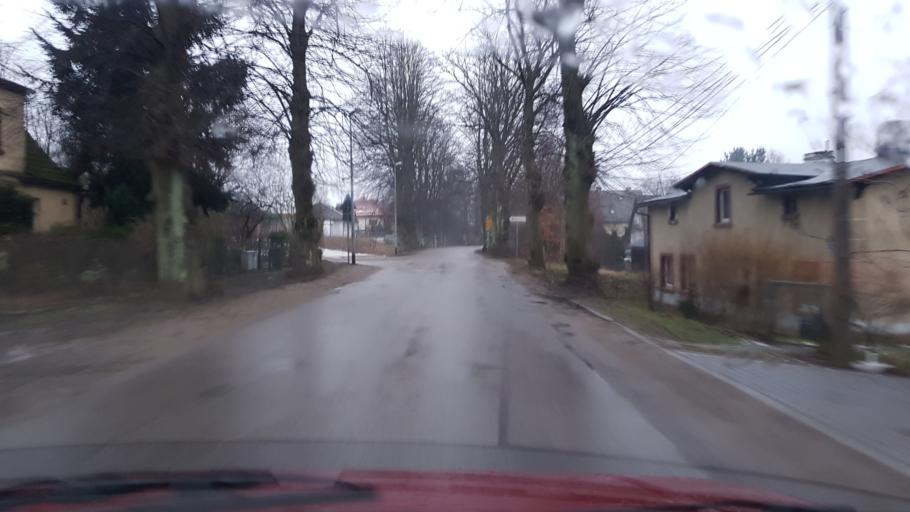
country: PL
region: West Pomeranian Voivodeship
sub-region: Powiat koszalinski
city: Sianow
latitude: 54.1846
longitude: 16.2442
